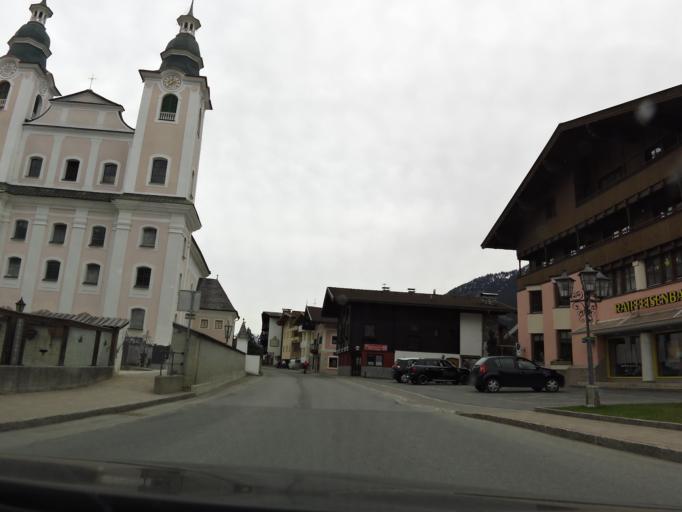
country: AT
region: Tyrol
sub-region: Politischer Bezirk Kitzbuhel
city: Brixen im Thale
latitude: 47.4503
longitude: 12.2497
